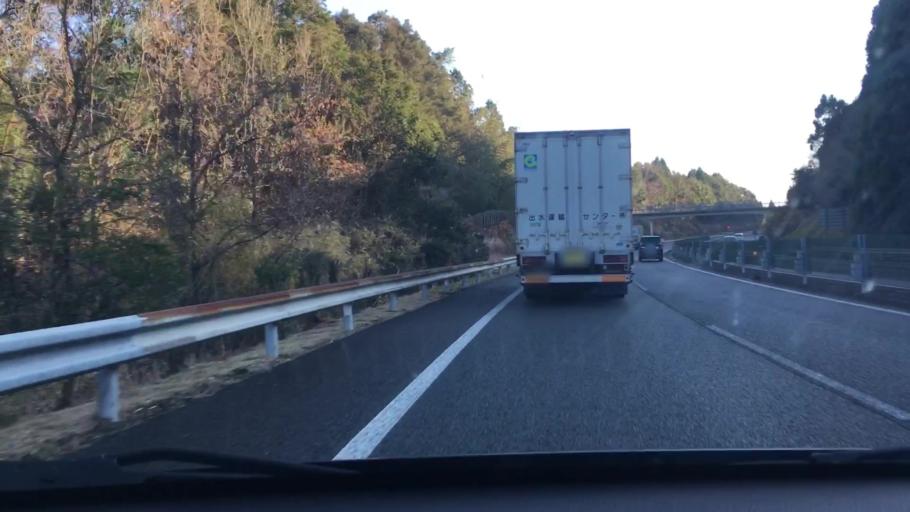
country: JP
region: Kagoshima
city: Kajiki
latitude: 31.8304
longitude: 130.6935
